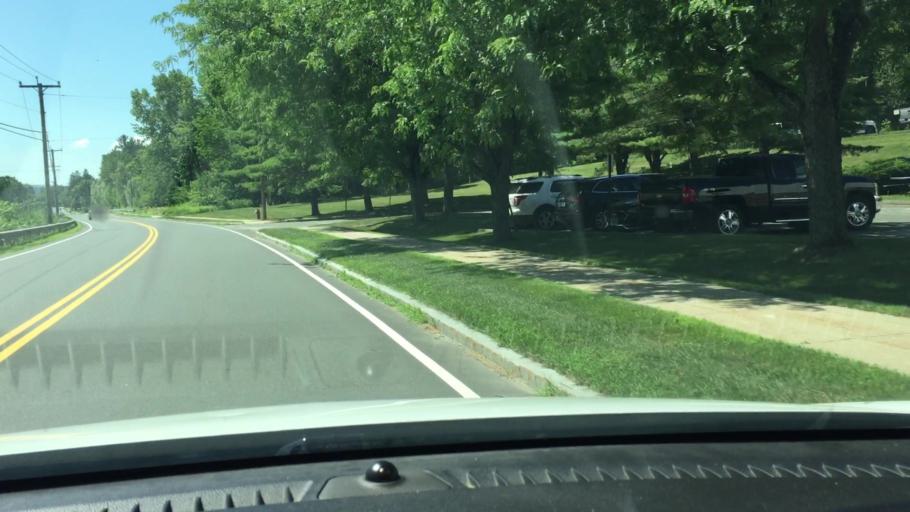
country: US
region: Massachusetts
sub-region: Berkshire County
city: Lenox
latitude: 42.3452
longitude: -73.2462
